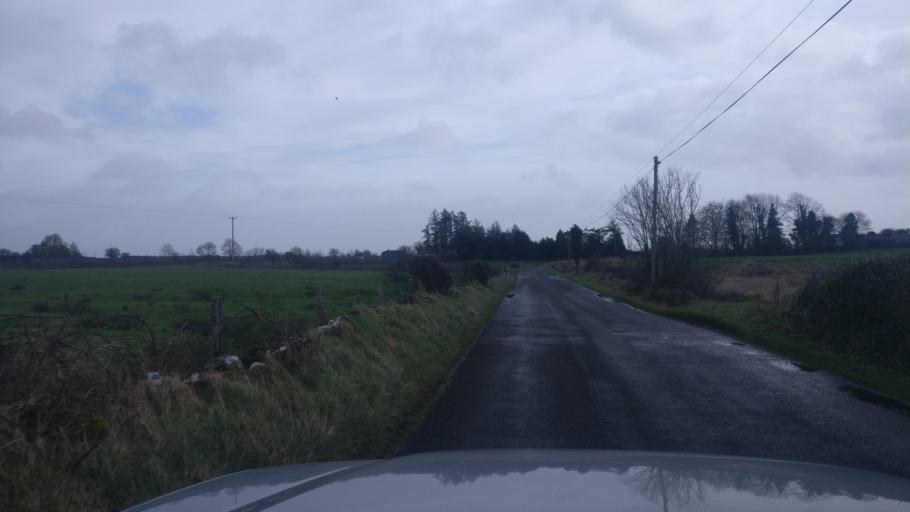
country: IE
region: Connaught
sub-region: County Galway
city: Loughrea
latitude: 53.2839
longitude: -8.4648
